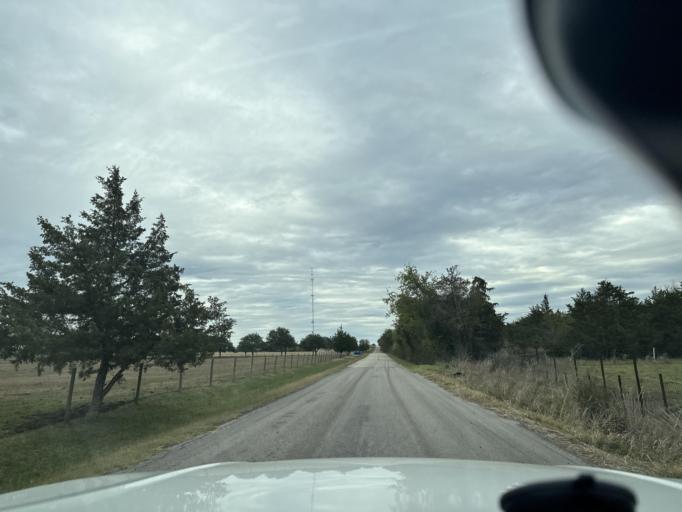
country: US
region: Texas
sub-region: Burleson County
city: Somerville
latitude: 30.1585
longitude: -96.6414
